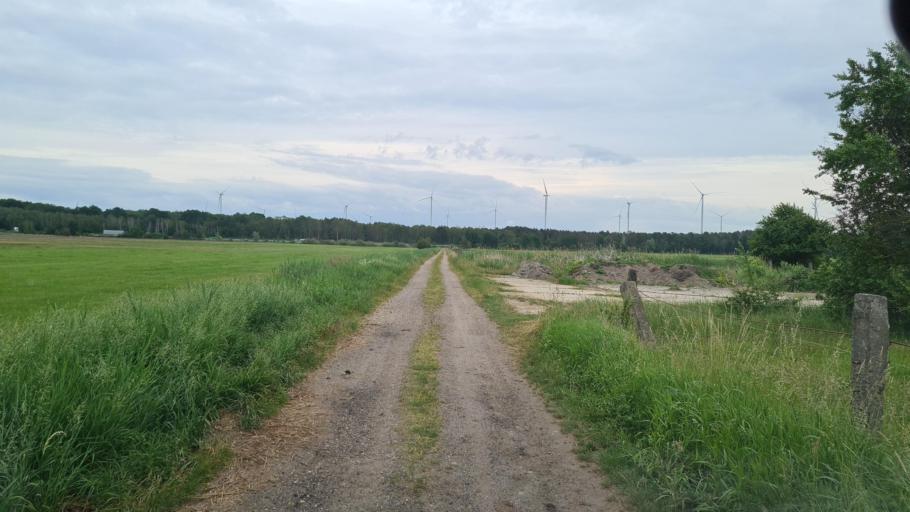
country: DE
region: Brandenburg
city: Bronkow
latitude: 51.6208
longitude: 13.9375
